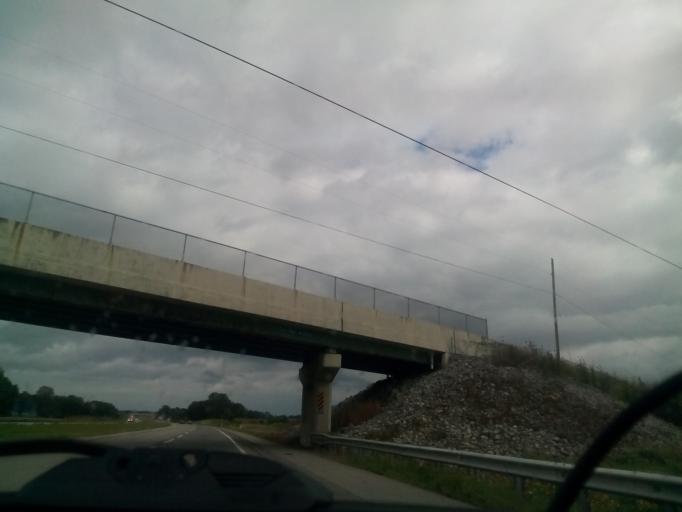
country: US
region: Indiana
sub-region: Steuben County
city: Fremont
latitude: 41.6943
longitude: -84.9078
